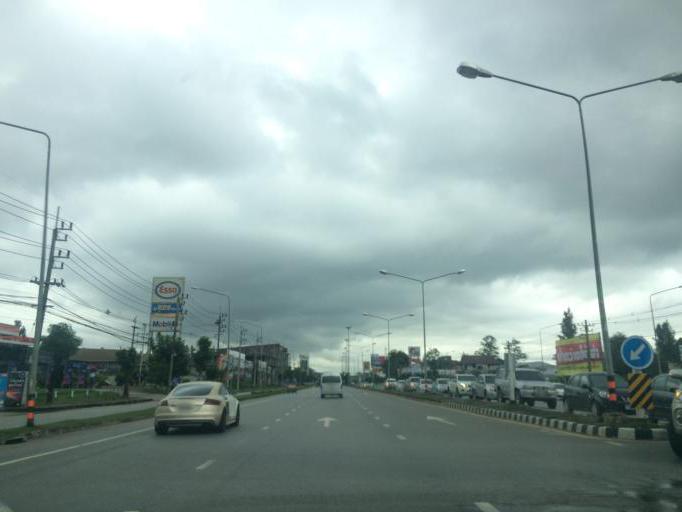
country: TH
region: Chiang Rai
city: Chiang Rai
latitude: 19.8818
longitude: 99.8340
